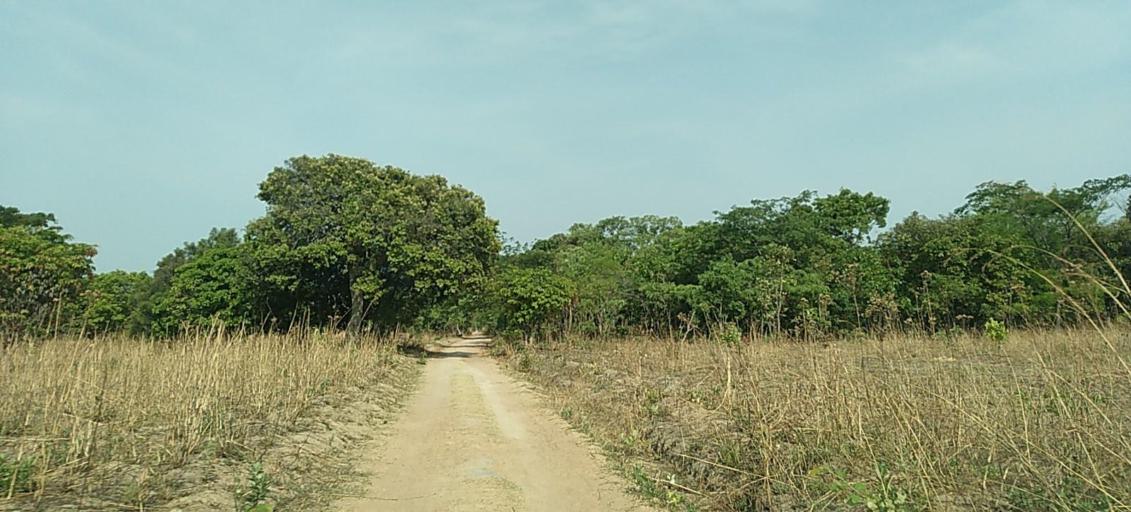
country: ZM
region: Copperbelt
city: Luanshya
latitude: -13.2190
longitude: 28.6578
